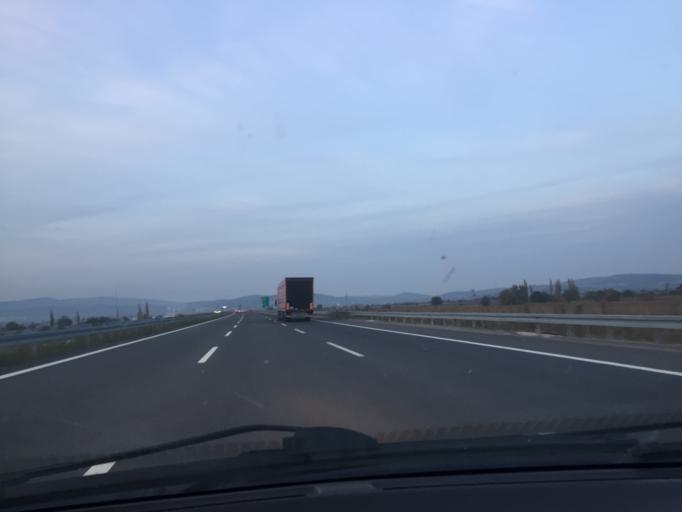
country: TR
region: Manisa
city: Halitpasa
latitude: 38.7518
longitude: 27.6600
